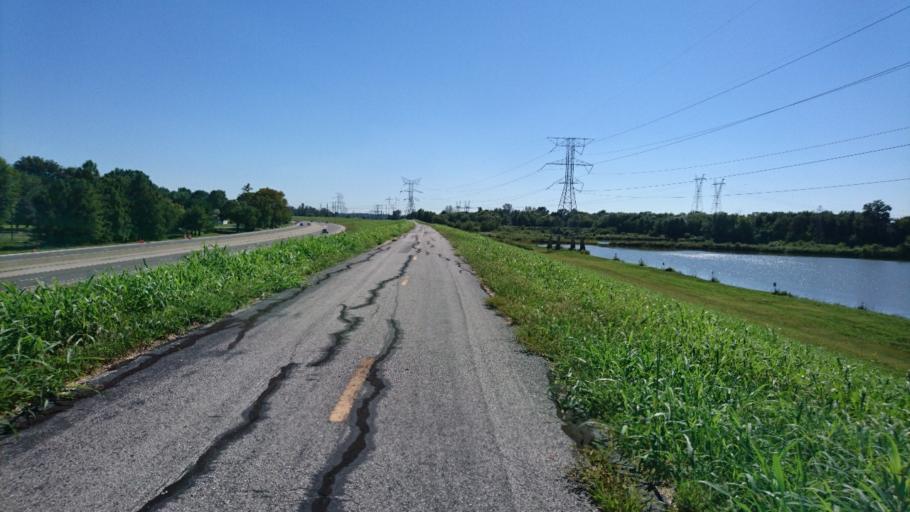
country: US
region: Illinois
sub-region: Madison County
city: Hartford
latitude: 38.8324
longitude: -90.1002
